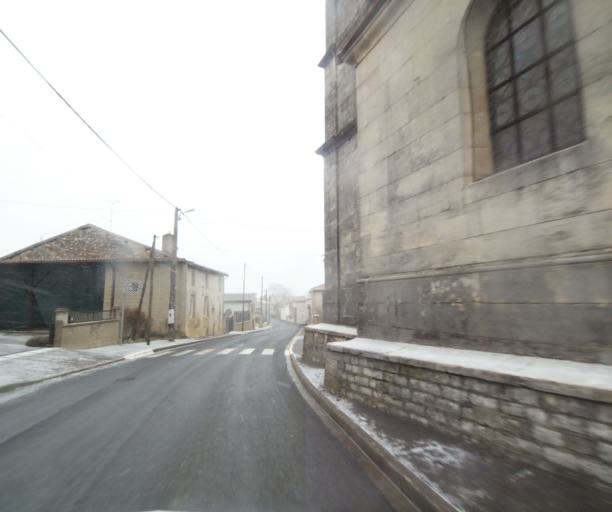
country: FR
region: Champagne-Ardenne
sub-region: Departement de la Haute-Marne
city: Wassy
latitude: 48.5130
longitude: 5.0052
